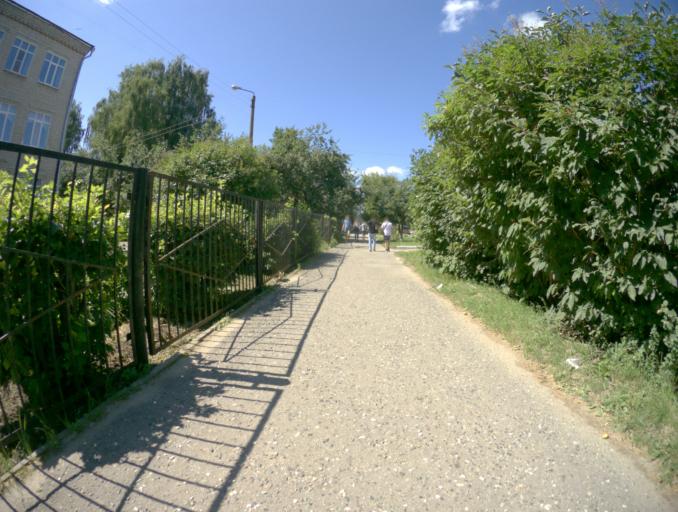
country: RU
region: Nizjnij Novgorod
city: Bor
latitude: 56.3563
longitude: 44.0681
